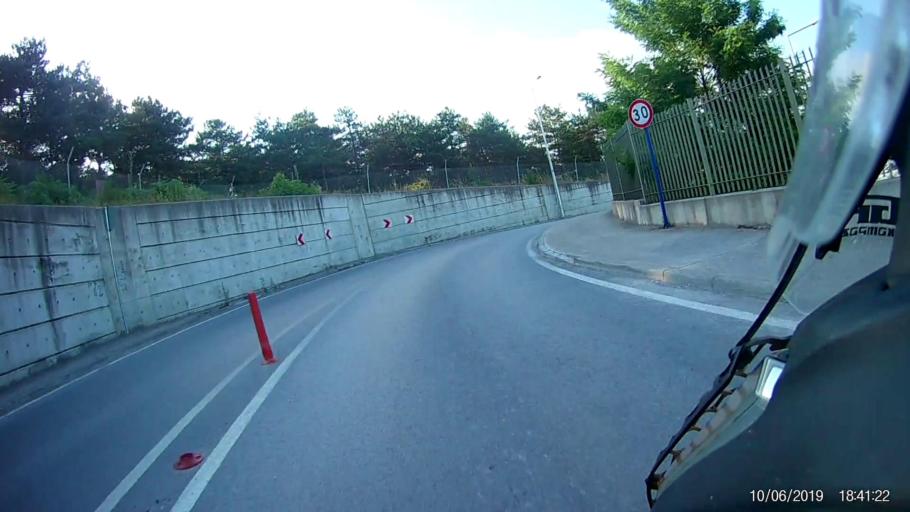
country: TR
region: Istanbul
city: Sancaktepe
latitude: 41.0333
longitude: 29.2559
